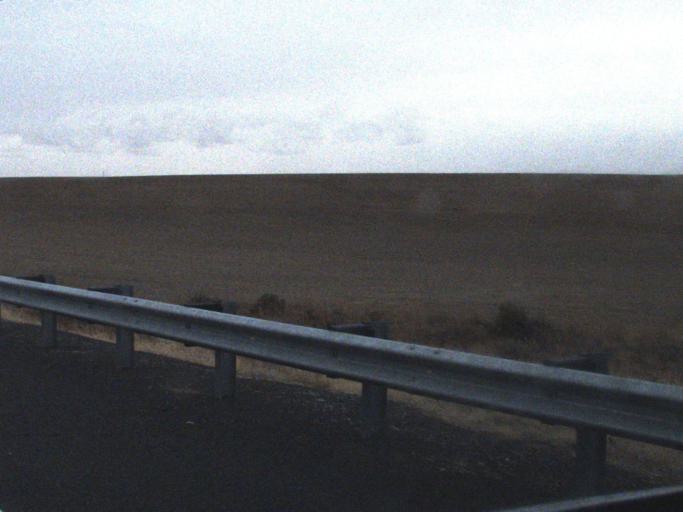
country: US
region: Washington
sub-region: Adams County
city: Ritzville
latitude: 46.7955
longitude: -118.4925
